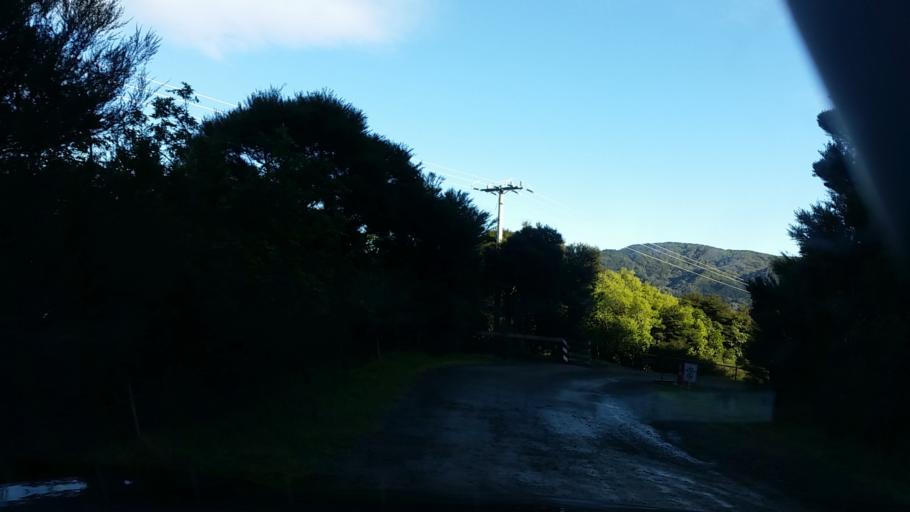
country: NZ
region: Marlborough
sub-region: Marlborough District
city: Picton
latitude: -40.9269
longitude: 173.8379
